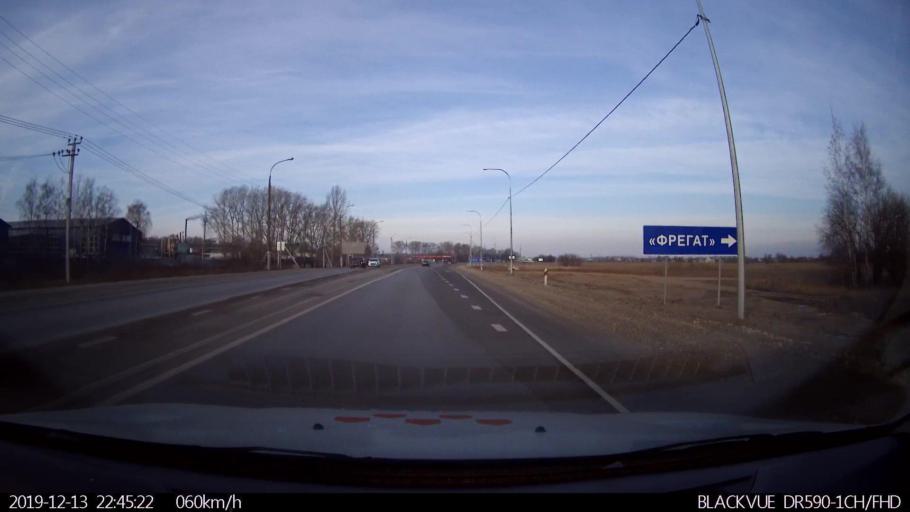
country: RU
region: Nizjnij Novgorod
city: Afonino
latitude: 56.2103
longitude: 44.1087
